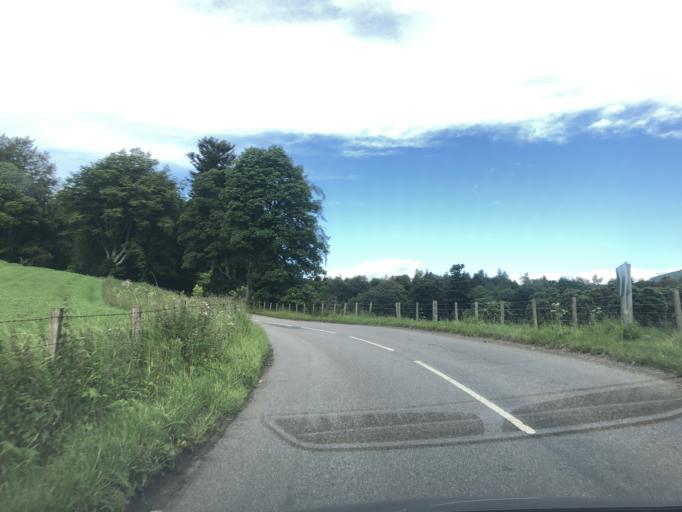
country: GB
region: Scotland
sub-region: Angus
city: Kirriemuir
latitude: 56.7118
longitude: -2.9800
